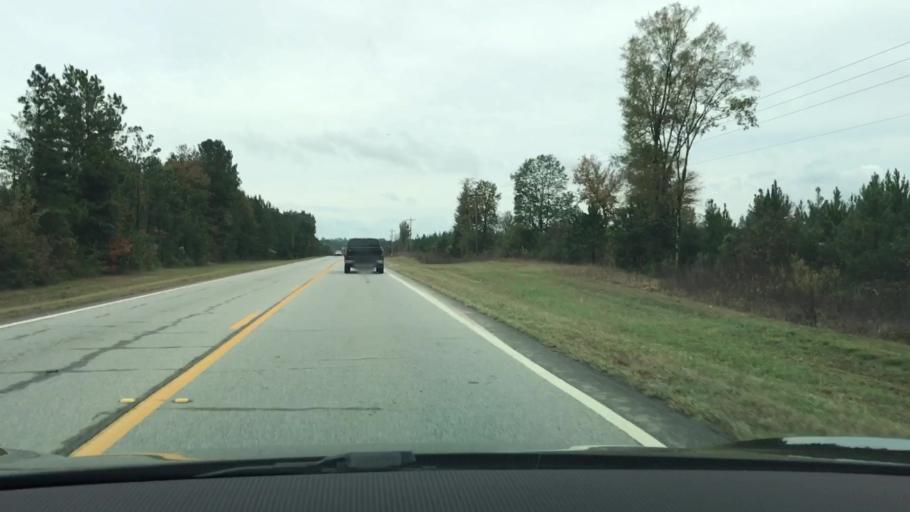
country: US
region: Georgia
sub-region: Greene County
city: Greensboro
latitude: 33.5999
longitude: -83.1971
